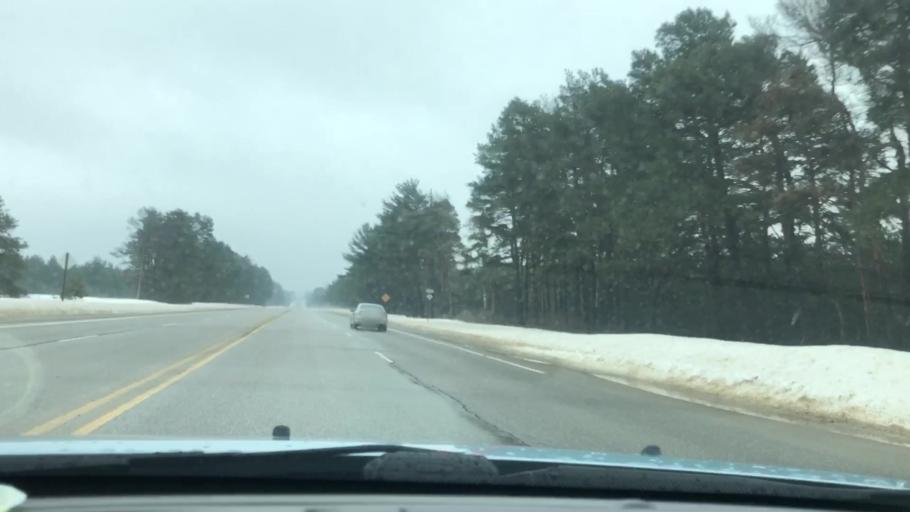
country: US
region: Michigan
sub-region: Otsego County
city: Gaylord
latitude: 45.0622
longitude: -84.8367
